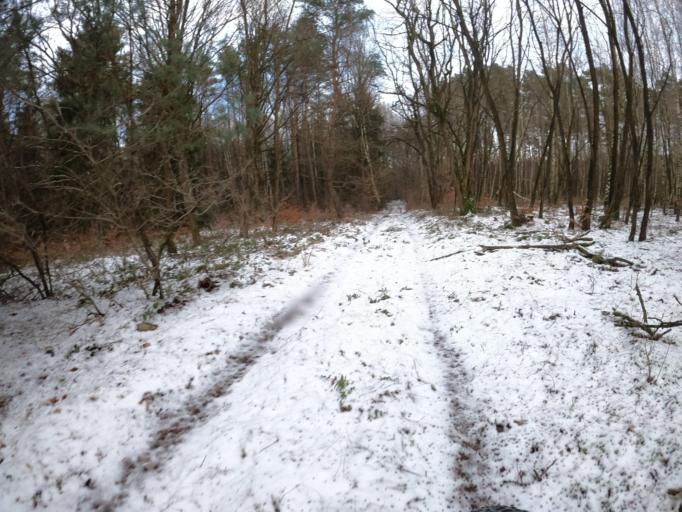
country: PL
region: Lubusz
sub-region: Powiat slubicki
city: Cybinka
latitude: 52.1908
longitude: 14.8717
